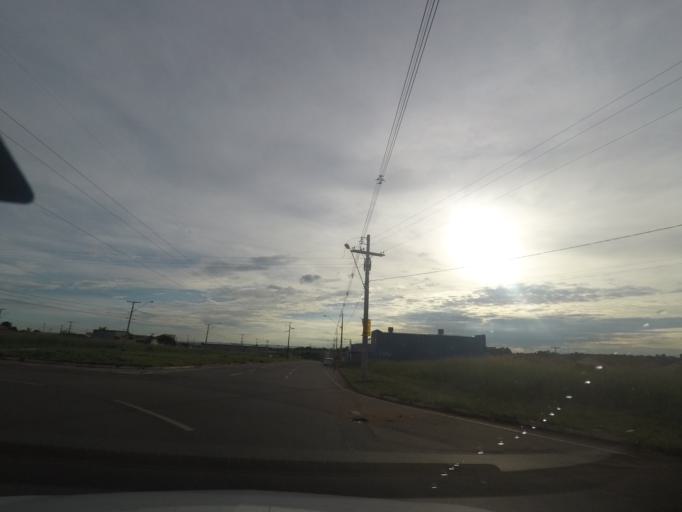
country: BR
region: Goias
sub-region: Trindade
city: Trindade
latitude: -16.7201
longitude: -49.3955
